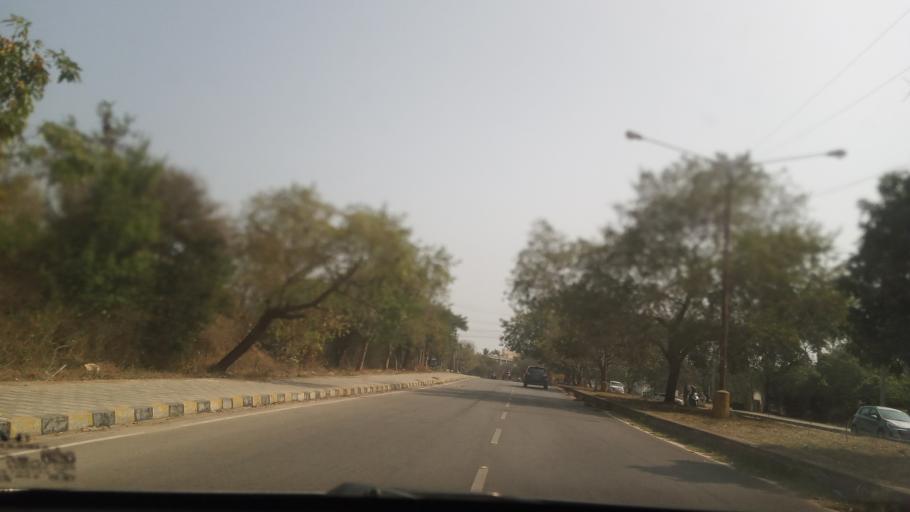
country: IN
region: Karnataka
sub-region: Mysore
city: Mysore
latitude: 12.2896
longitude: 76.6212
